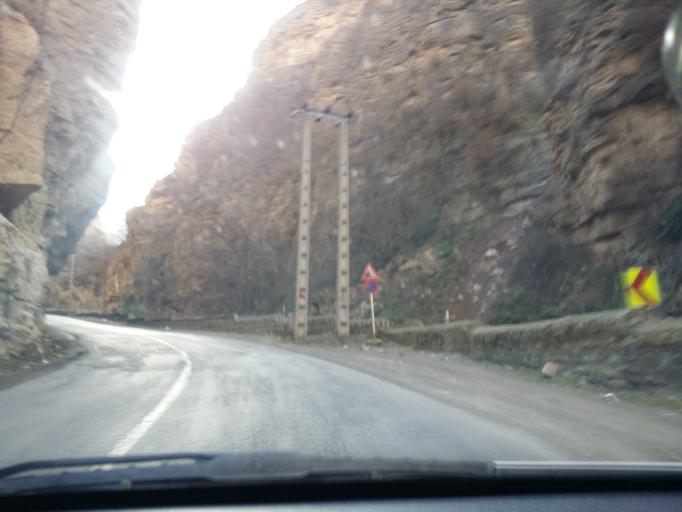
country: IR
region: Mazandaran
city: Chalus
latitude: 36.2714
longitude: 51.2456
